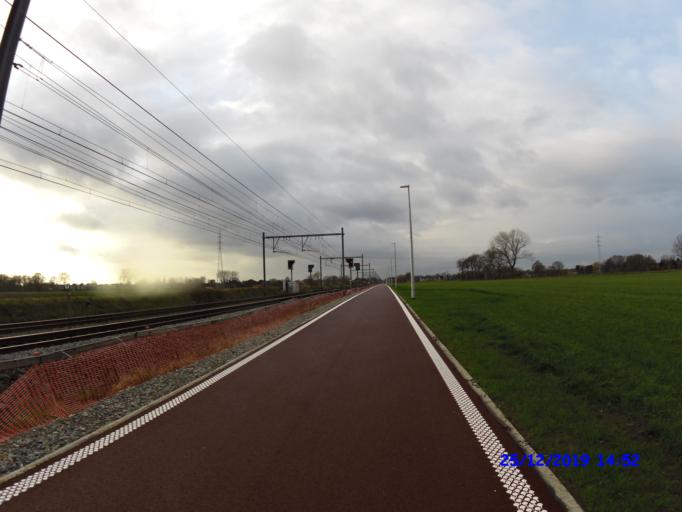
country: BE
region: Flanders
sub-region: Provincie Antwerpen
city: Geel
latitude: 51.1692
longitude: 4.9569
